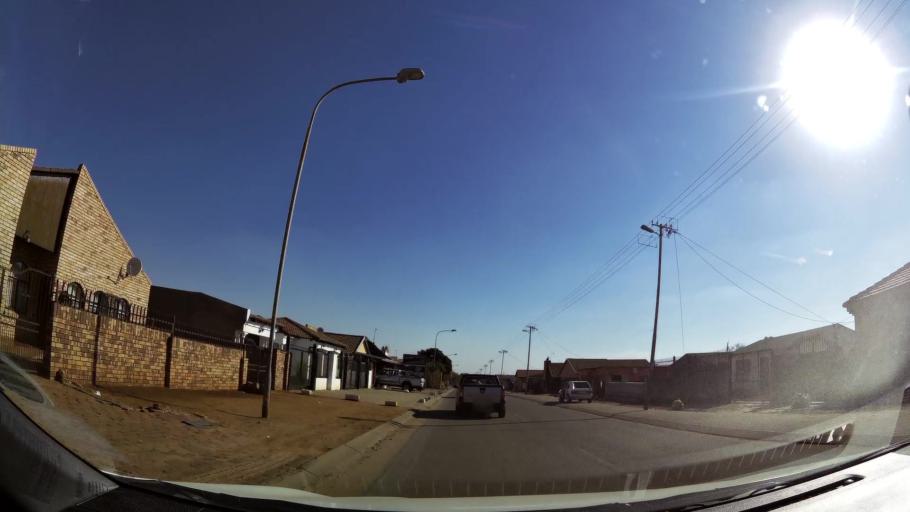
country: ZA
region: Gauteng
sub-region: City of Tshwane Metropolitan Municipality
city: Cullinan
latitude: -25.7121
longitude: 28.3893
